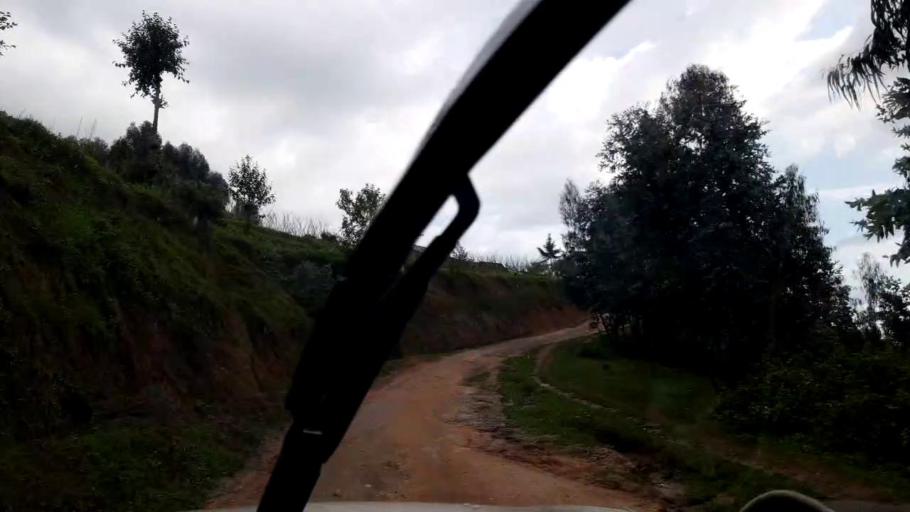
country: RW
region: Southern Province
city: Gitarama
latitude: -1.8662
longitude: 29.5685
